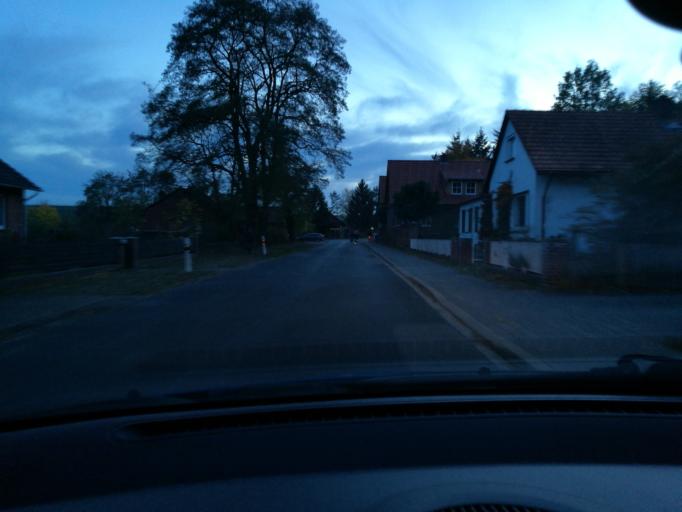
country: DE
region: Lower Saxony
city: Gartow
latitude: 53.0575
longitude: 11.4548
